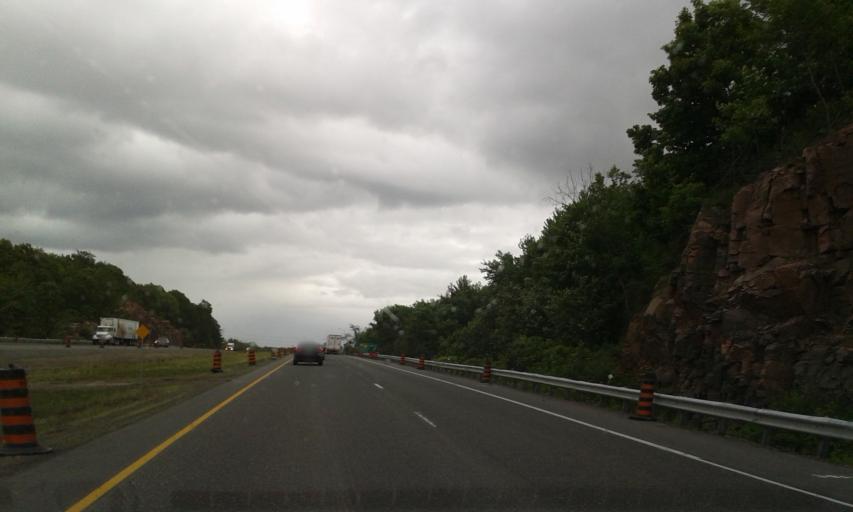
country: US
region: New York
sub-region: Jefferson County
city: Alexandria Bay
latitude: 44.3782
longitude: -76.0173
